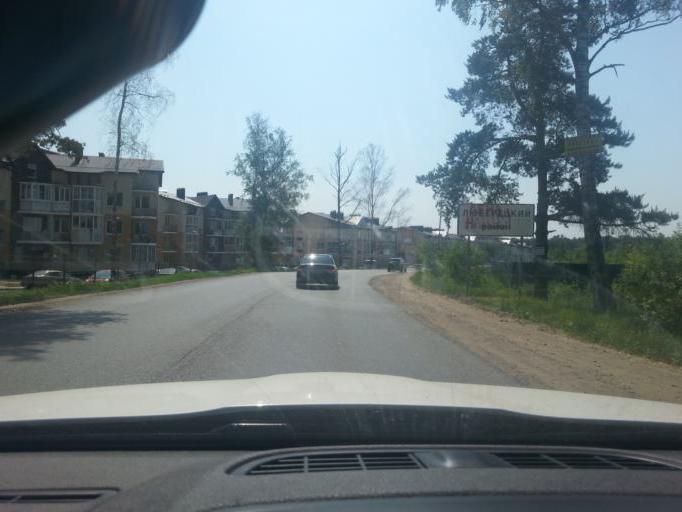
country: RU
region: Moskovskaya
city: Zheleznodorozhnyy
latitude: 55.7155
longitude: 37.9737
